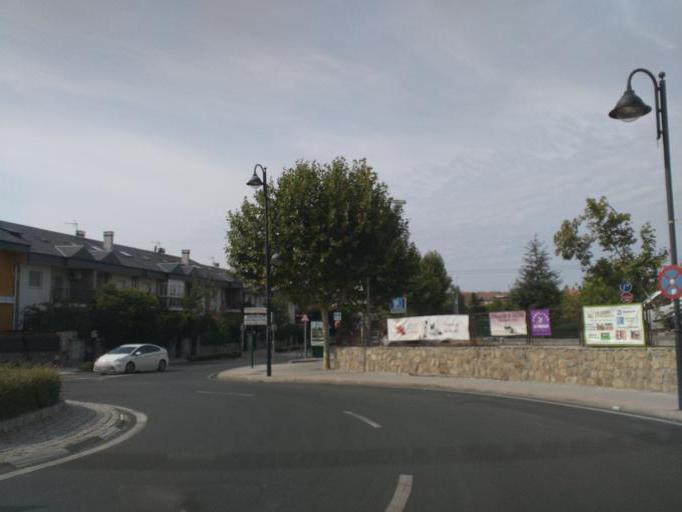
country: ES
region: Madrid
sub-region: Provincia de Madrid
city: Galapagar
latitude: 40.5833
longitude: -3.9967
